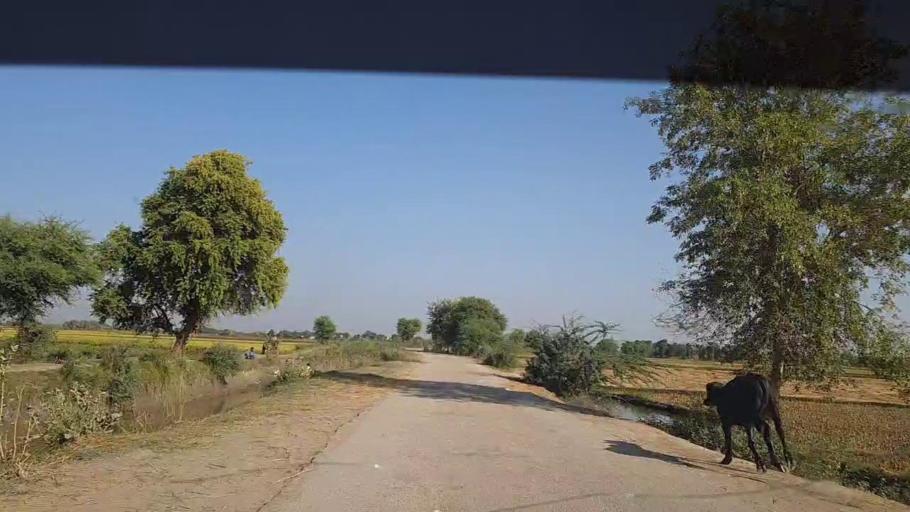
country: PK
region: Sindh
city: Larkana
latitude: 27.6233
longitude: 68.2398
